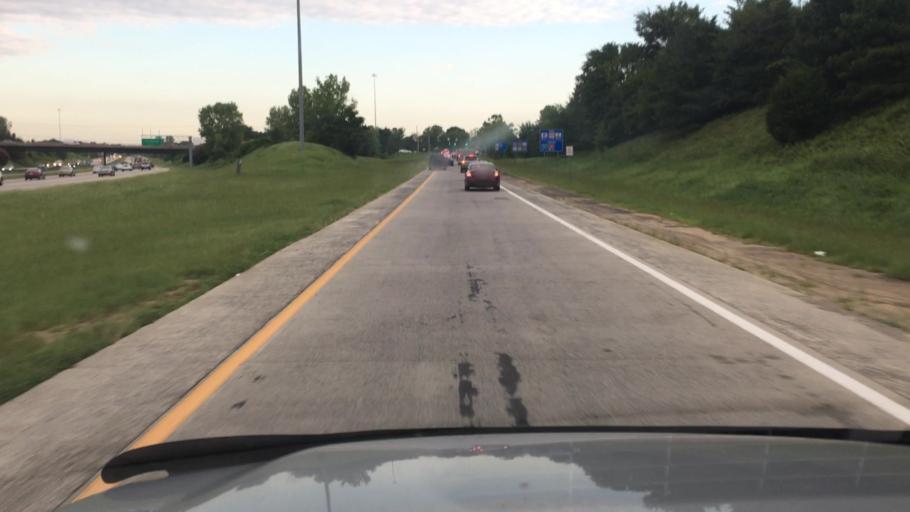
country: US
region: North Carolina
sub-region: Mecklenburg County
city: Pineville
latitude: 35.1396
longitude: -80.9284
